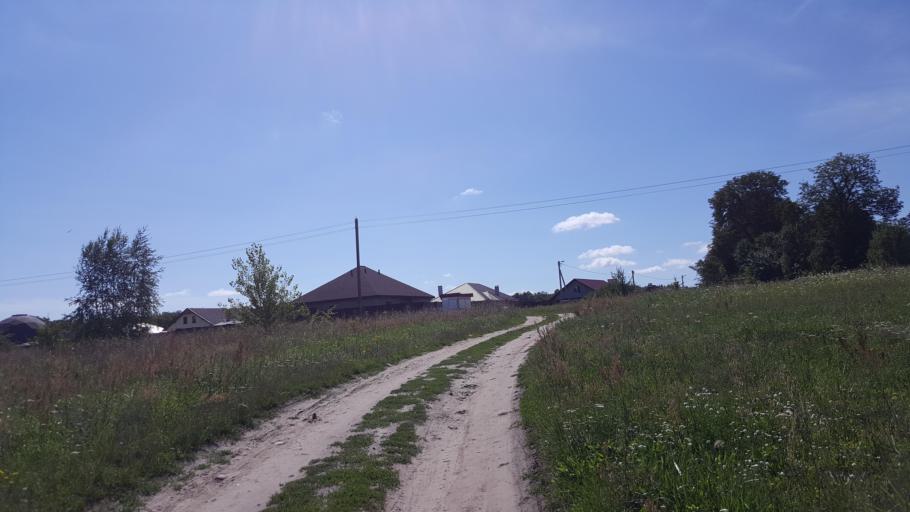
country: BY
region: Brest
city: Charnawchytsy
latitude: 52.2710
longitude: 23.7627
